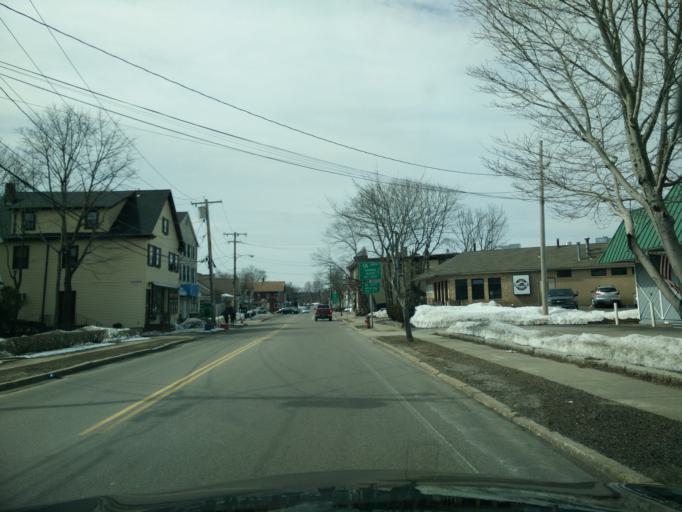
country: US
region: Massachusetts
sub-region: Norfolk County
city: Walpole
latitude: 42.1471
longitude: -71.2507
